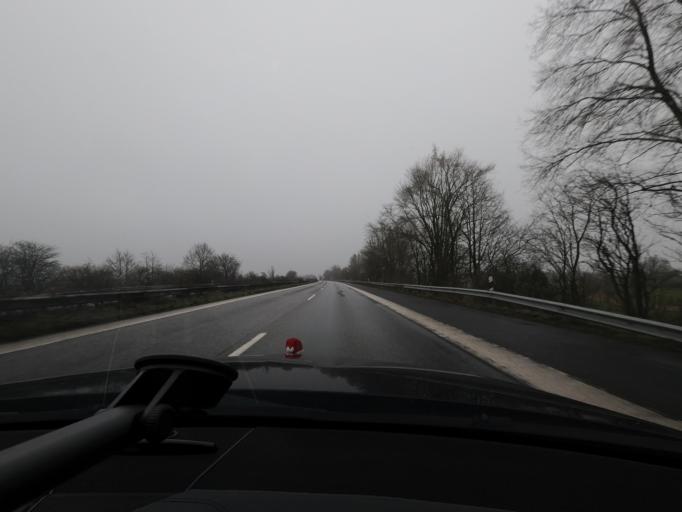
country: DE
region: Schleswig-Holstein
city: Brekendorf
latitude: 54.4249
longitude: 9.6005
